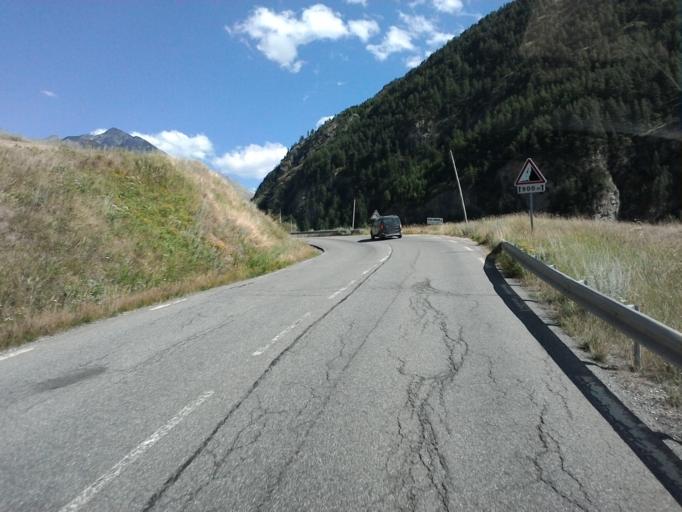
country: FR
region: Rhone-Alpes
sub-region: Departement de la Savoie
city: Valloire
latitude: 45.0421
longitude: 6.3398
